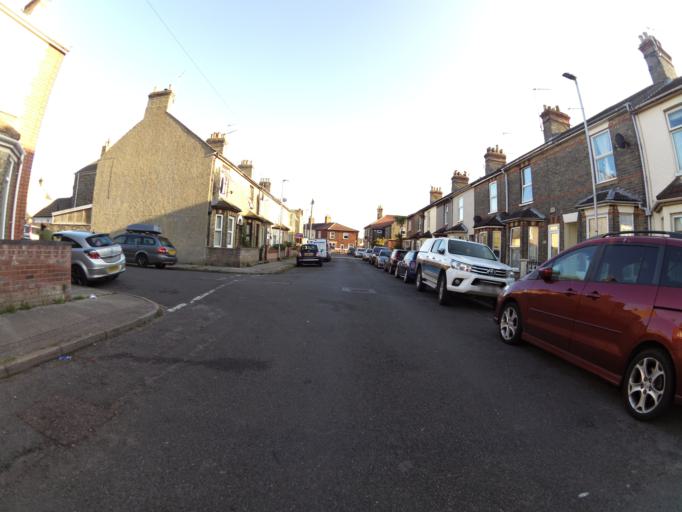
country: GB
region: England
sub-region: Suffolk
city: Lowestoft
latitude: 52.4675
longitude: 1.7392
